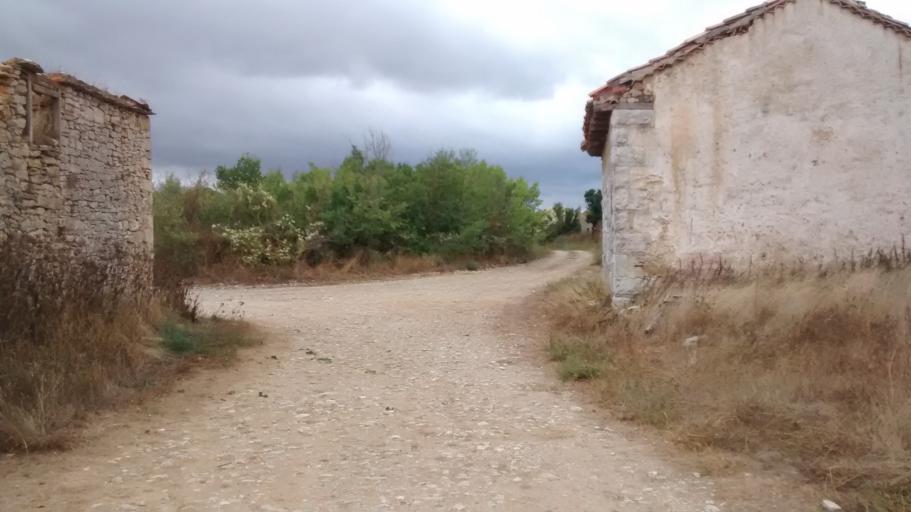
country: ES
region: Castille and Leon
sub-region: Provincia de Palencia
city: Berzosilla
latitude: 42.7690
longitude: -3.9903
